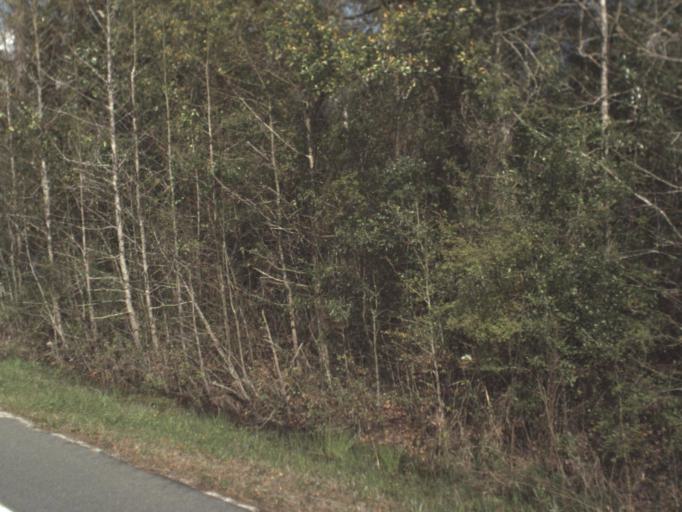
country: US
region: Florida
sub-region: Wakulla County
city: Crawfordville
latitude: 30.0186
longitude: -84.5005
